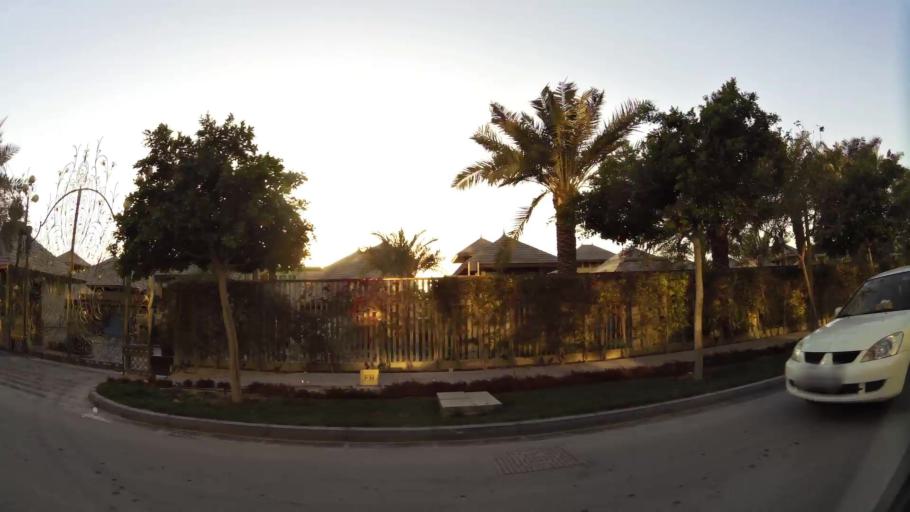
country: BH
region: Manama
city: Jidd Hafs
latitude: 26.2419
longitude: 50.5672
